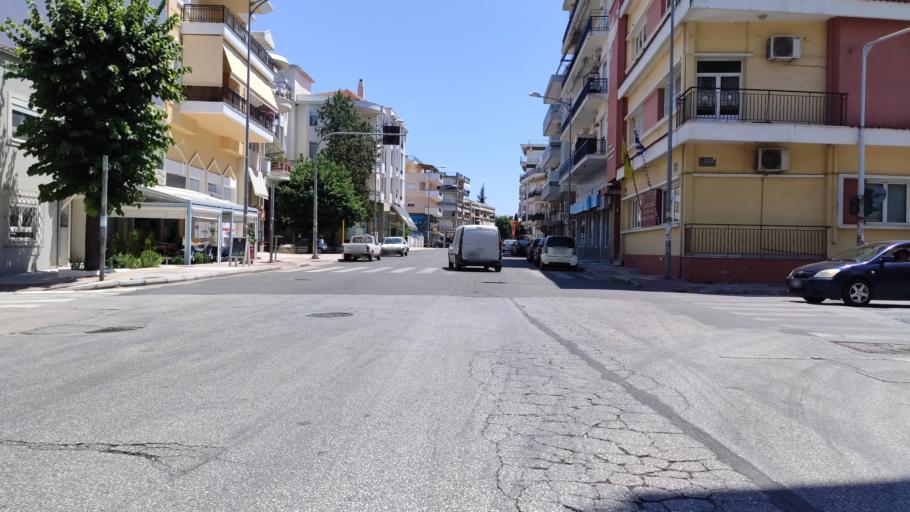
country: GR
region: East Macedonia and Thrace
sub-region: Nomos Rodopis
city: Komotini
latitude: 41.1146
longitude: 25.4091
